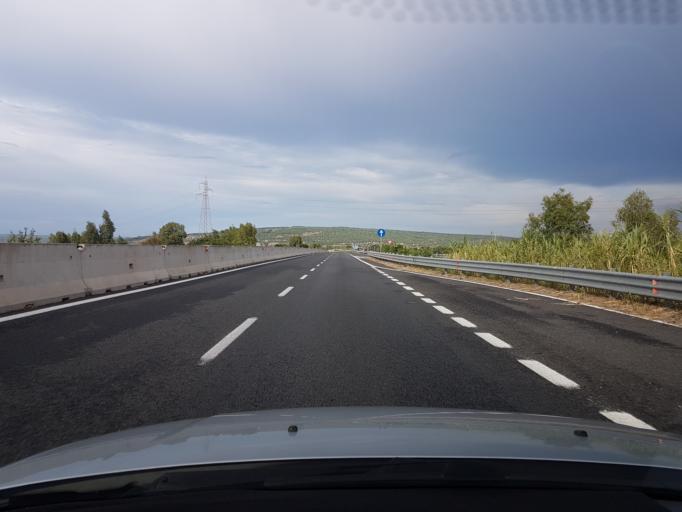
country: IT
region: Sardinia
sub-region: Provincia di Oristano
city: Tramatza
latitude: 39.9947
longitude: 8.6504
